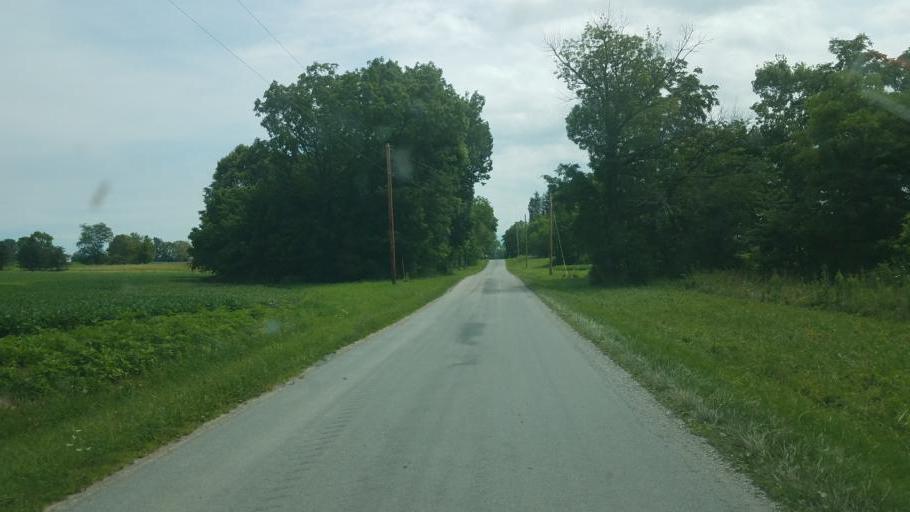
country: US
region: Ohio
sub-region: Wyandot County
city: Upper Sandusky
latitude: 40.8770
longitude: -83.1483
